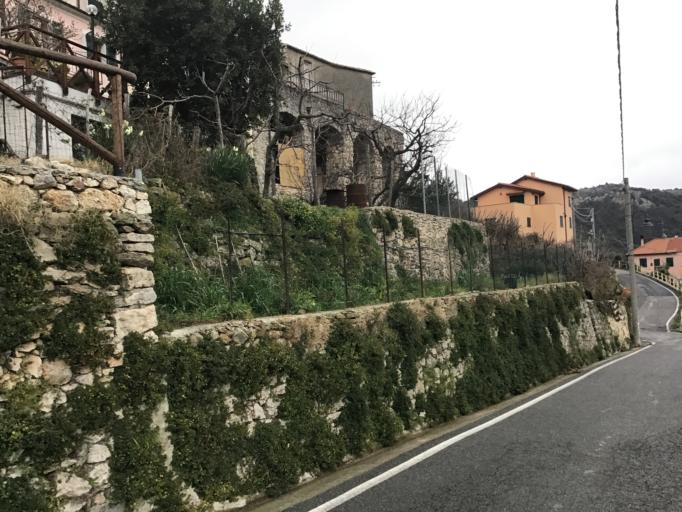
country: IT
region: Liguria
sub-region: Provincia di Savona
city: Orco Feglino
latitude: 44.2208
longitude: 8.3379
